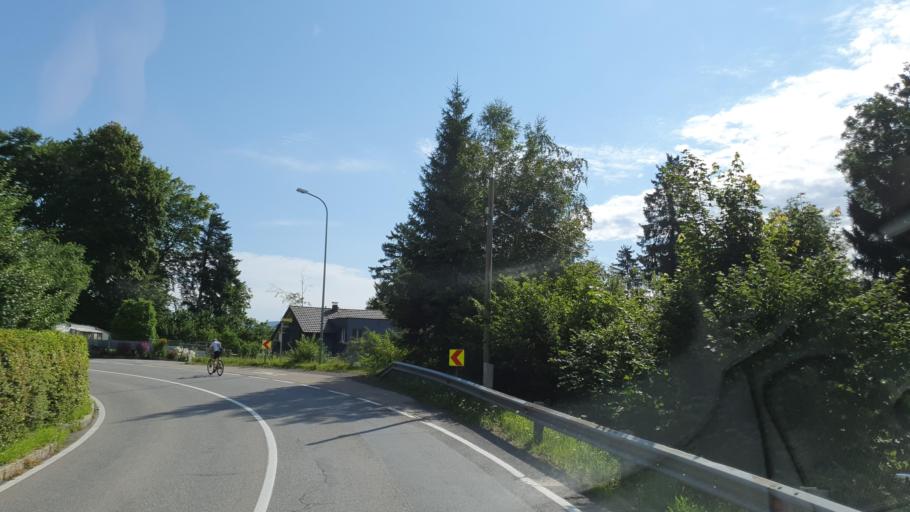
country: AT
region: Vorarlberg
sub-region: Politischer Bezirk Bregenz
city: Kennelbach
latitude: 47.4930
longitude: 9.7925
